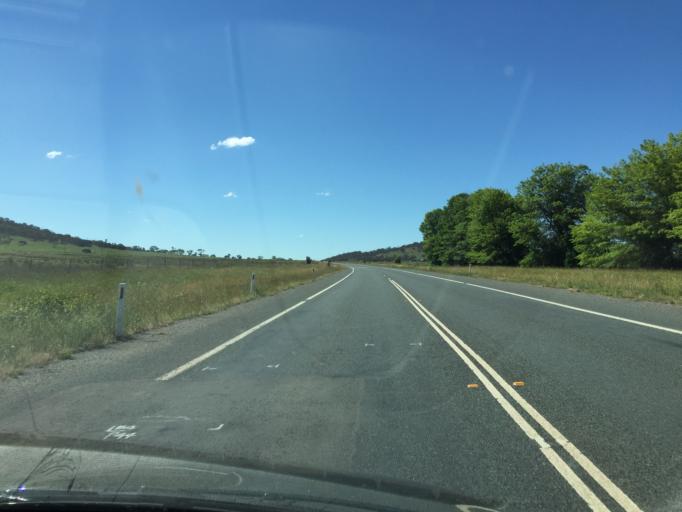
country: AU
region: Australian Capital Territory
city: Macarthur
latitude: -35.4894
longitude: 149.1500
